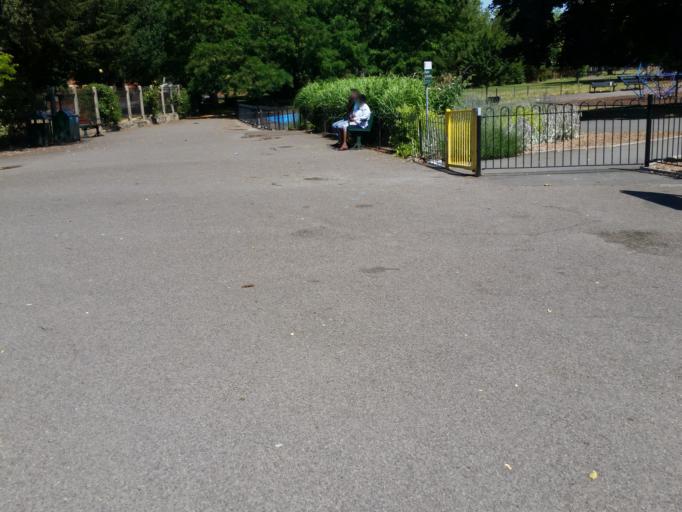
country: GB
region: England
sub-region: Greater London
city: Harringay
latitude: 51.5998
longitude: -0.0759
